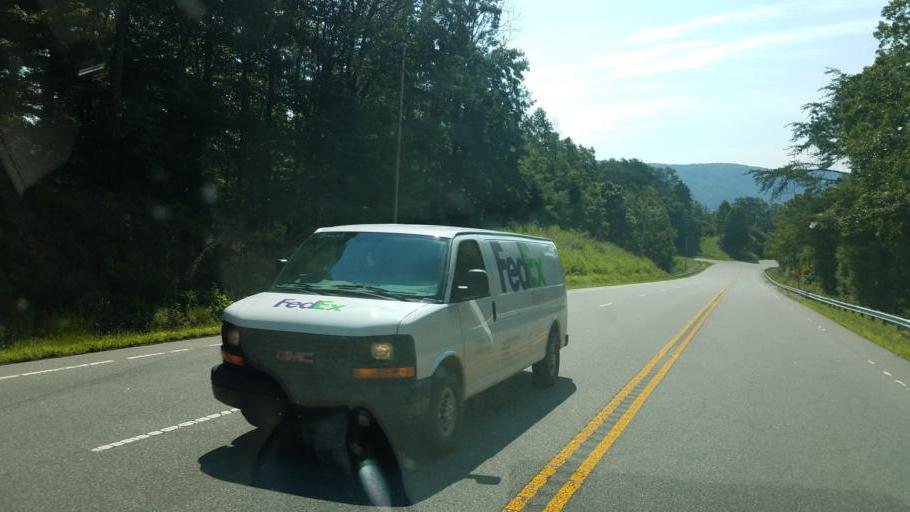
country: US
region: North Carolina
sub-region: Burke County
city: Glen Alpine
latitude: 35.9181
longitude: -81.8135
